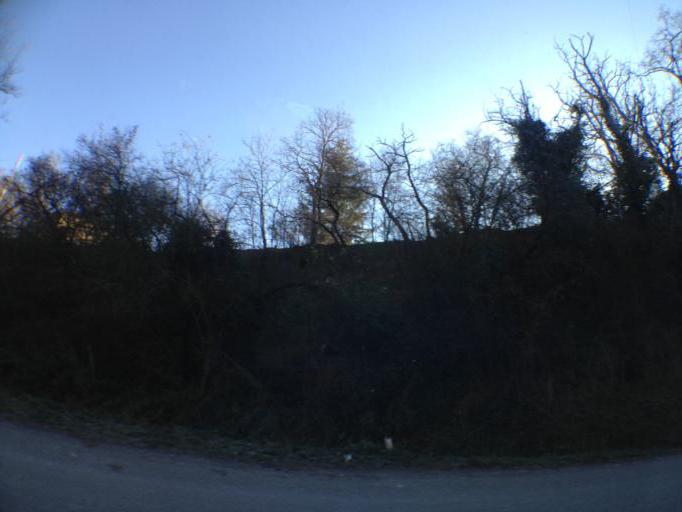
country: IT
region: Umbria
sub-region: Provincia di Perugia
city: Norcia
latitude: 42.7986
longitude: 13.1002
